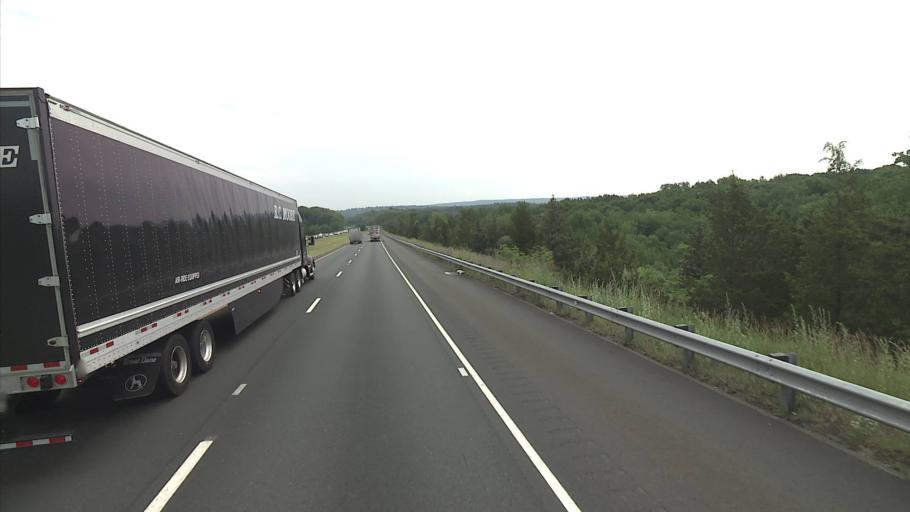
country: US
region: Connecticut
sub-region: New Haven County
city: Middlebury
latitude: 41.5170
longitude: -73.1095
